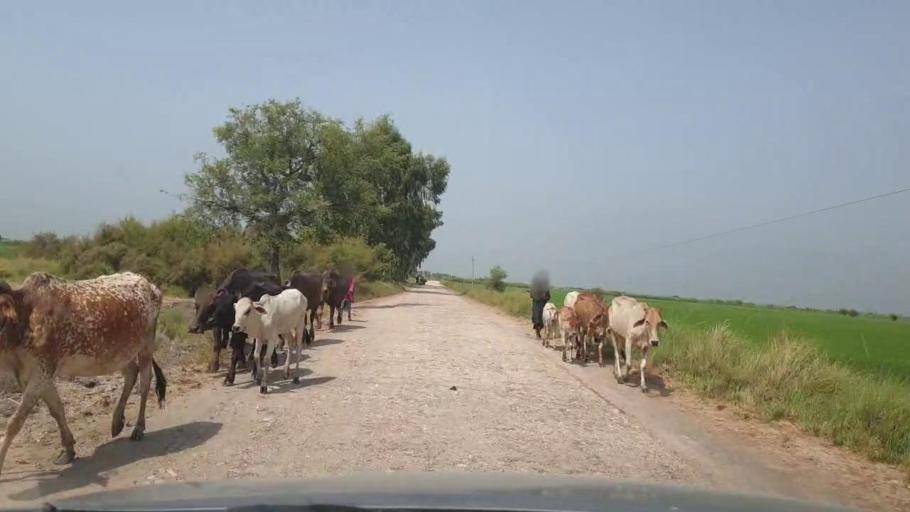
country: PK
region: Sindh
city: Garhi Yasin
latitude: 27.9092
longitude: 68.3962
